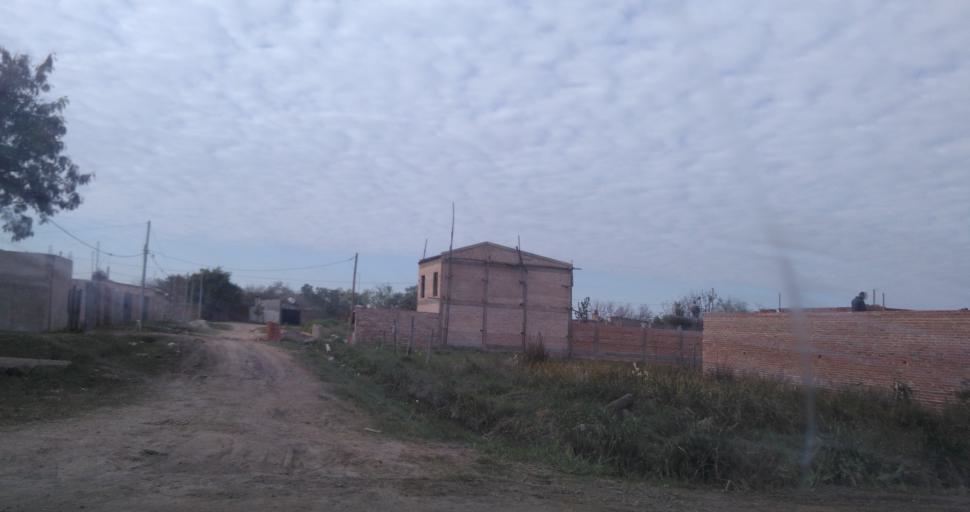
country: AR
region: Chaco
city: Fontana
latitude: -27.4461
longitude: -59.0337
